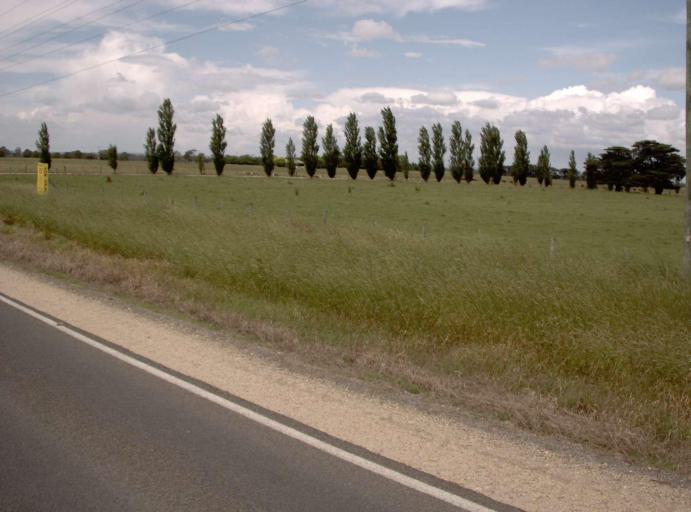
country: AU
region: Victoria
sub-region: Wellington
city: Sale
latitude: -38.0186
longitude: 147.0099
